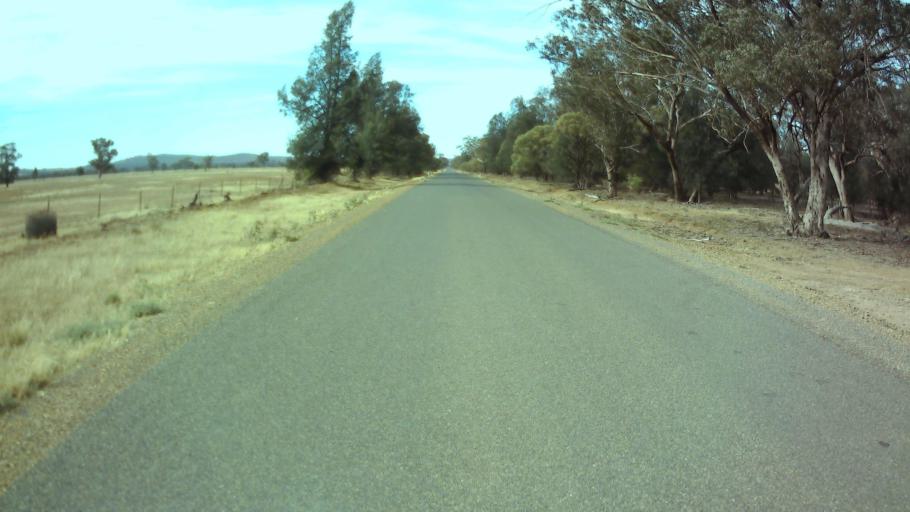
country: AU
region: New South Wales
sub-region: Weddin
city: Grenfell
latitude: -33.8799
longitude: 147.8563
